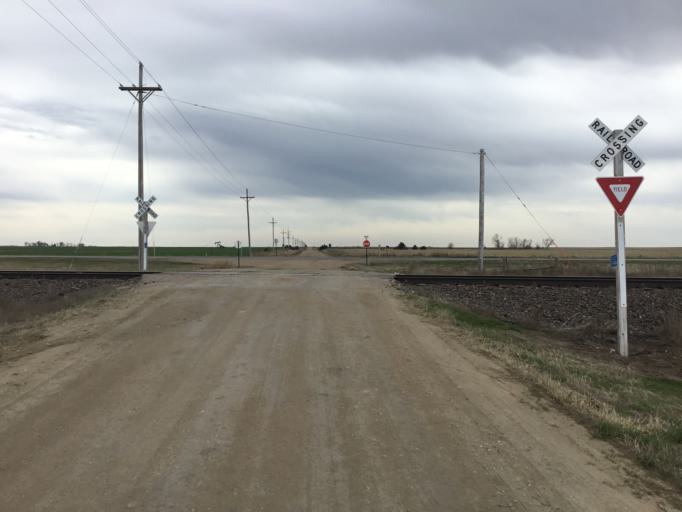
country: US
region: Kansas
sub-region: Russell County
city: Russell
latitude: 38.8836
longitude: -98.9468
